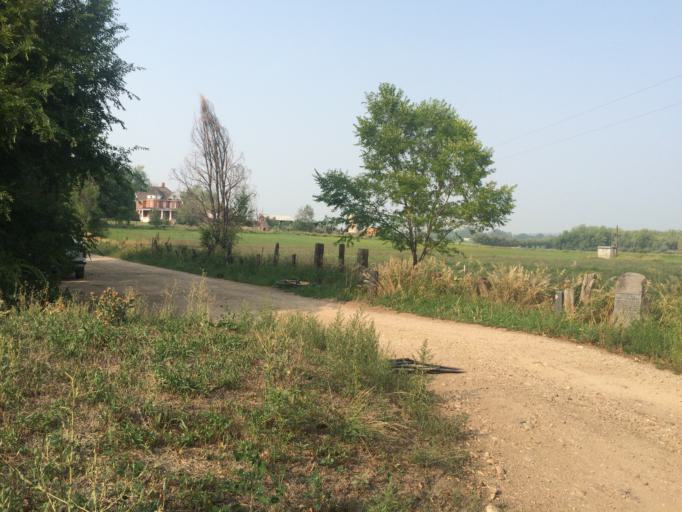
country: US
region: Colorado
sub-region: Boulder County
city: Gunbarrel
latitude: 40.0437
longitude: -105.2070
